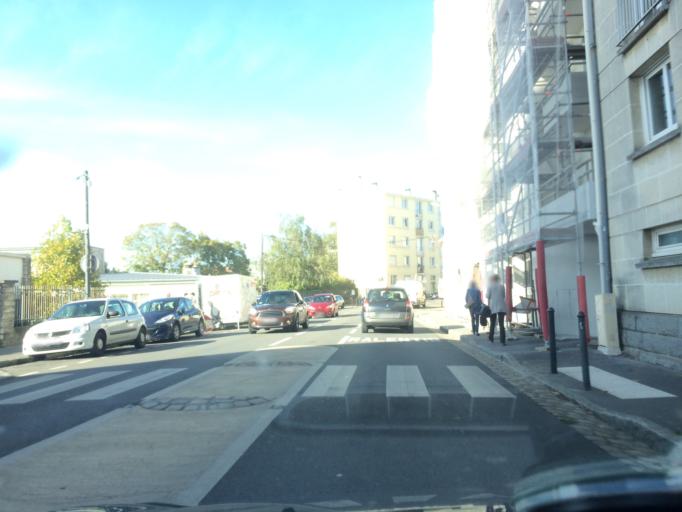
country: FR
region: Pays de la Loire
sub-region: Departement de la Loire-Atlantique
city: Nantes
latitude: 47.2326
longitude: -1.5425
